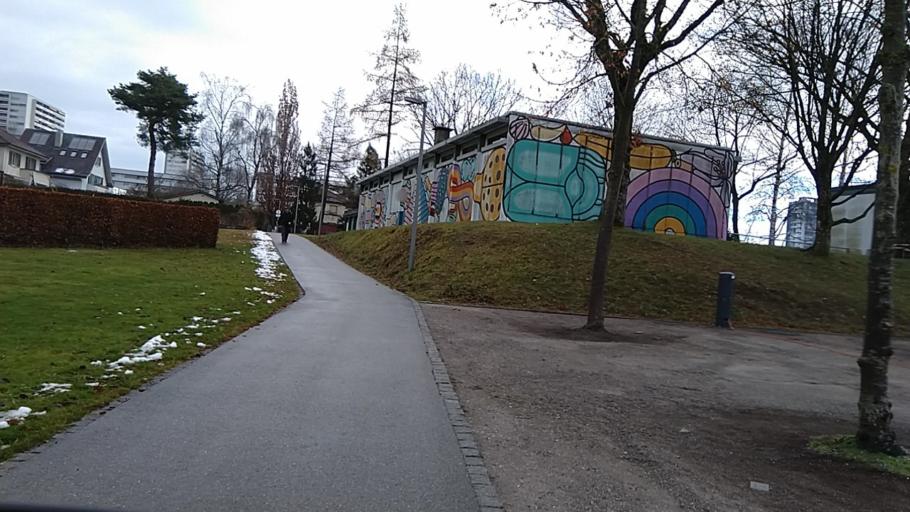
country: CH
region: Bern
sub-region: Bern-Mittelland District
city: Wohlen
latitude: 46.9468
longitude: 7.3811
